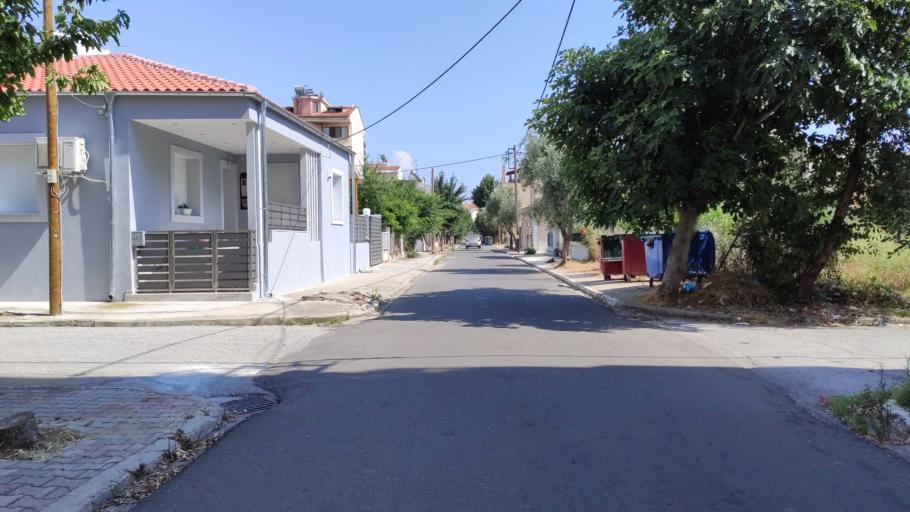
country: GR
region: East Macedonia and Thrace
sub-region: Nomos Rodopis
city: Komotini
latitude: 41.1142
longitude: 25.3924
